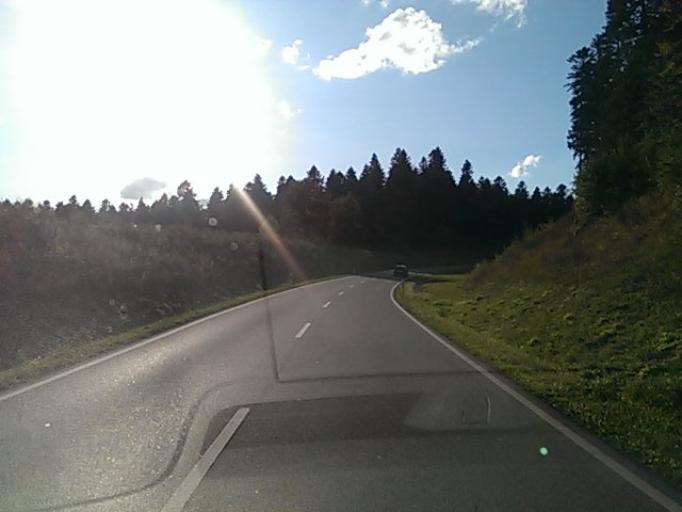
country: DE
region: Baden-Wuerttemberg
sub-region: Karlsruhe Region
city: Lossburg
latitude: 48.3583
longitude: 8.4598
